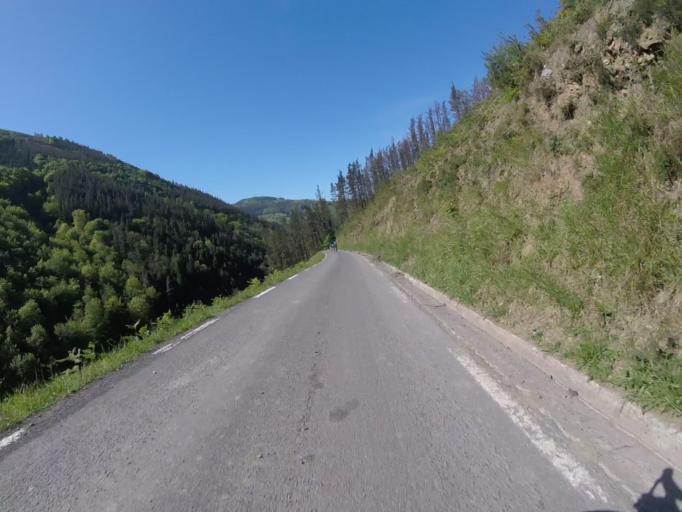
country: ES
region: Basque Country
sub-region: Provincia de Guipuzcoa
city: Errezil
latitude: 43.1863
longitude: -2.1982
